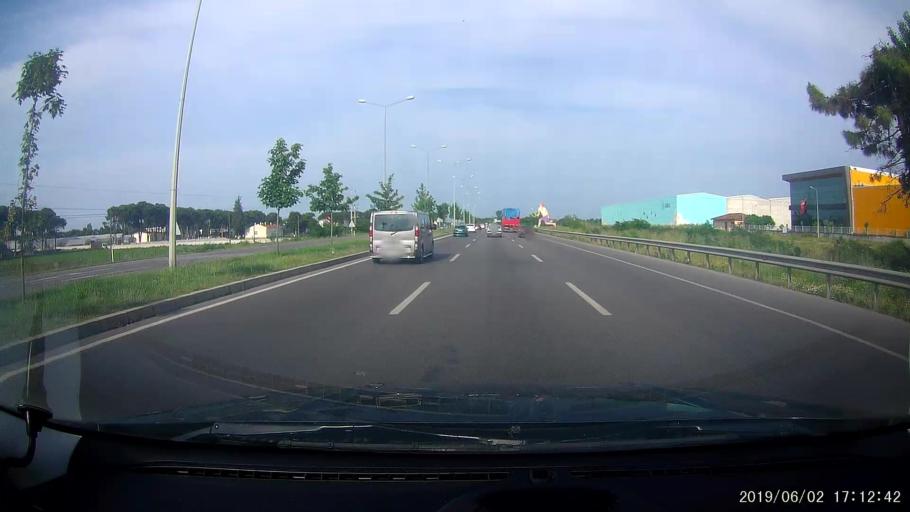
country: TR
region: Samsun
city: Tekkekoy
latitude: 41.2293
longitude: 36.4940
